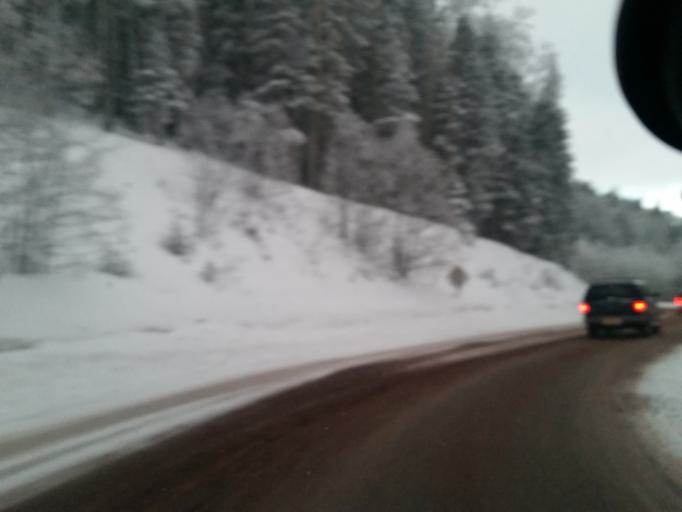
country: US
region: New Mexico
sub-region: Santa Fe County
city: Santa Fe
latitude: 35.7603
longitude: -105.8122
